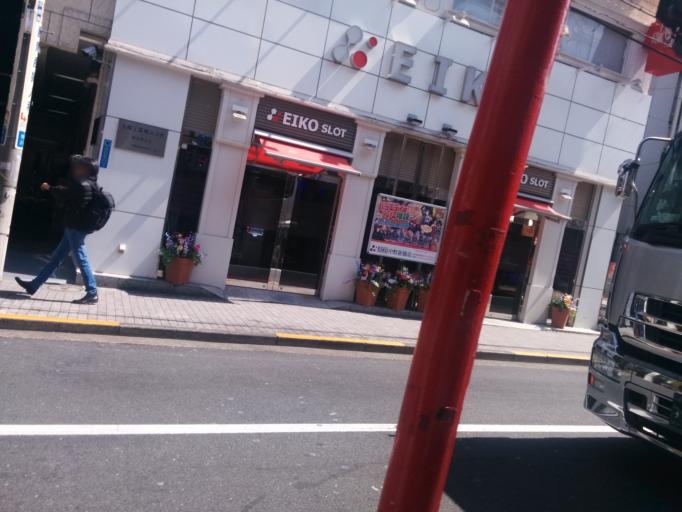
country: JP
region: Tokyo
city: Tokyo
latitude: 35.6919
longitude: 139.6745
